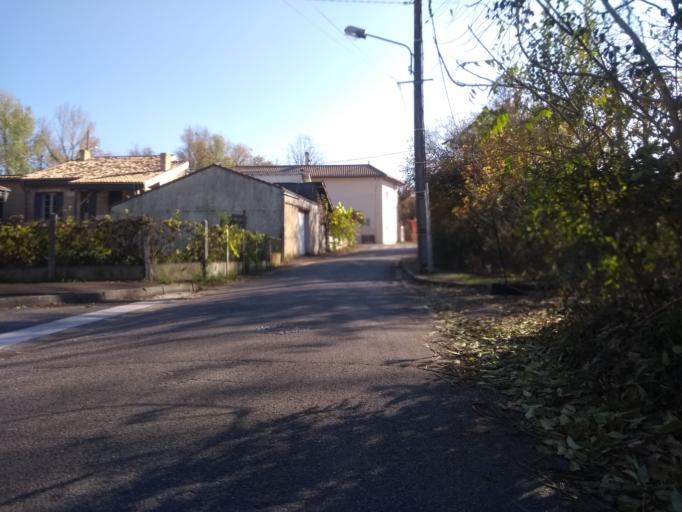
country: FR
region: Aquitaine
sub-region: Departement de la Gironde
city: Leognan
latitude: 44.7300
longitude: -0.5945
